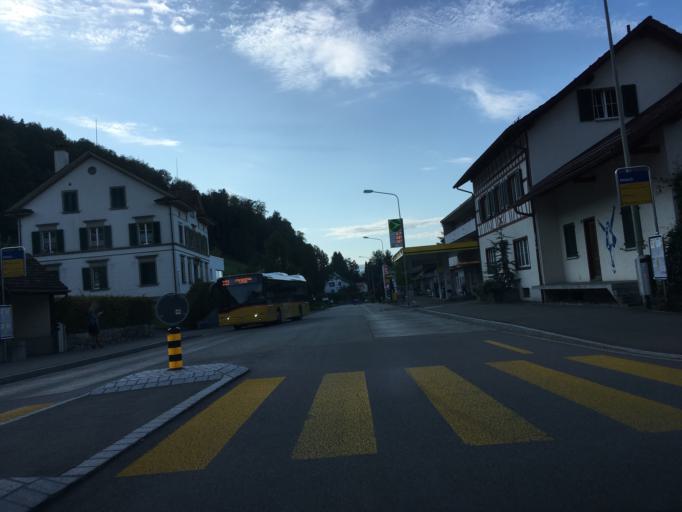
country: CH
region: Zurich
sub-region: Bezirk Affoltern
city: Hausen am Albis / Hausen (Dorf)
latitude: 47.2490
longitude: 8.5299
